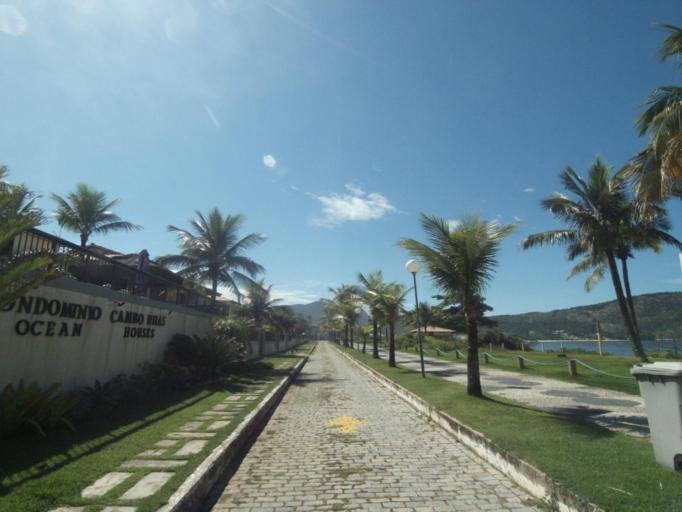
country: BR
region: Rio de Janeiro
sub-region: Niteroi
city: Niteroi
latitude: -22.9613
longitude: -43.0564
